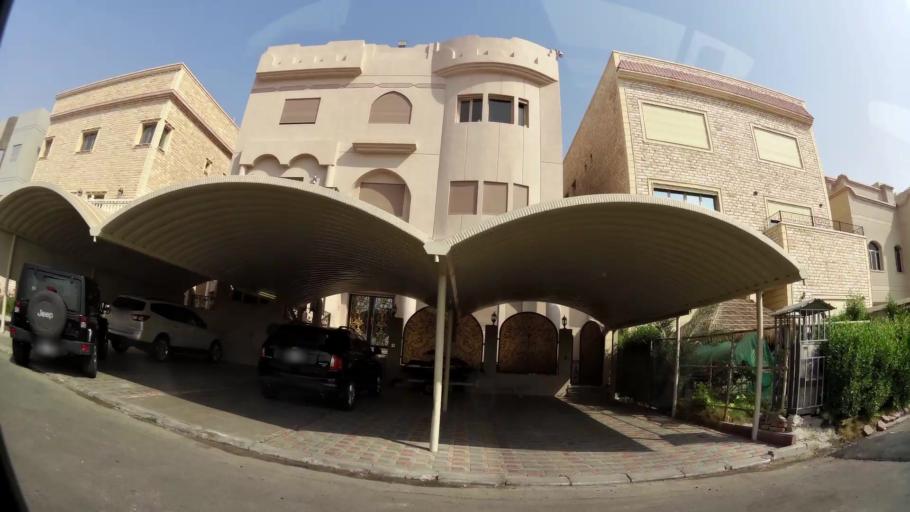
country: KW
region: Muhafazat al Jahra'
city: Al Jahra'
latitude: 29.3273
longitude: 47.7700
